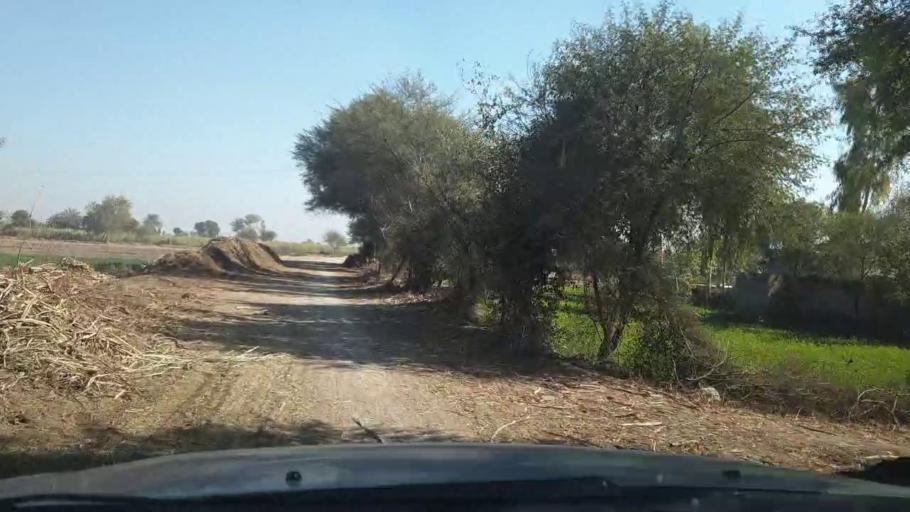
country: PK
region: Sindh
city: Ghotki
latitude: 28.0298
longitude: 69.2117
